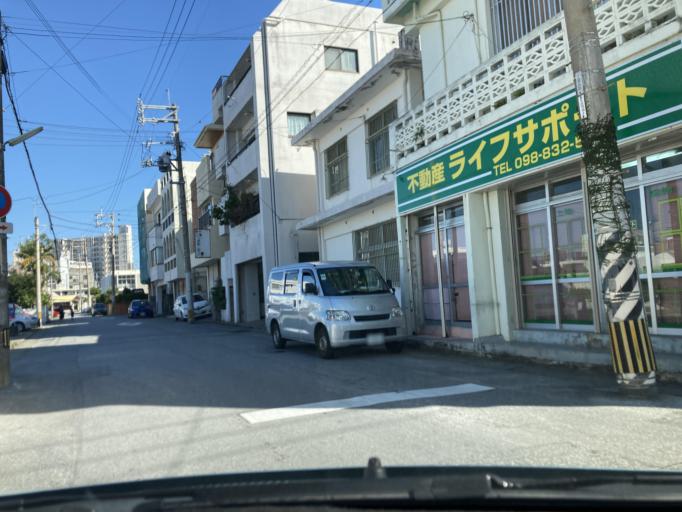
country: JP
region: Okinawa
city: Naha-shi
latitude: 26.2098
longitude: 127.6859
